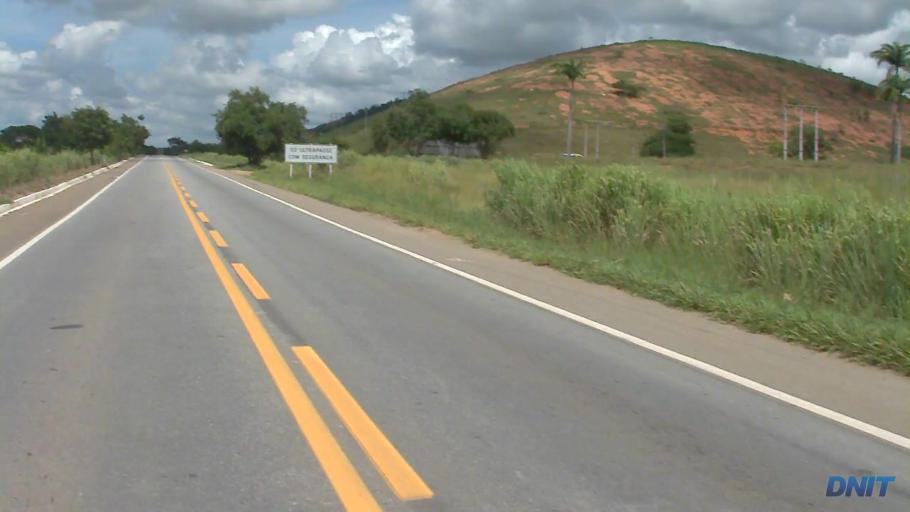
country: BR
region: Minas Gerais
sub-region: Governador Valadares
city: Governador Valadares
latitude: -18.9434
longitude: -42.0626
